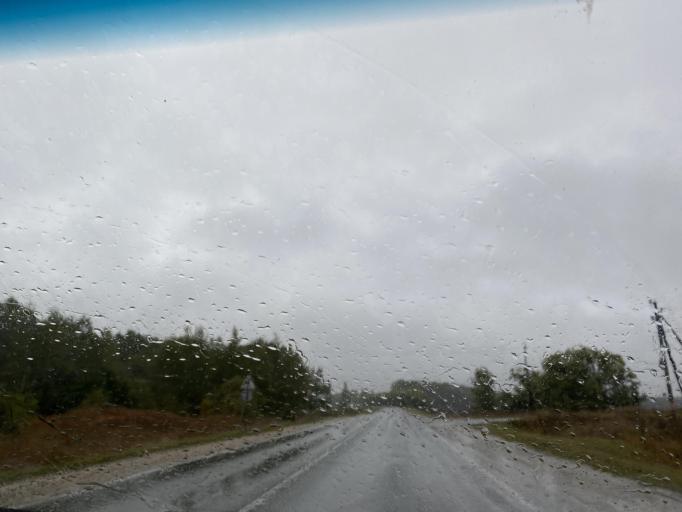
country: RU
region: Rjazan
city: Starozhilovo
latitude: 54.3855
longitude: 39.9250
